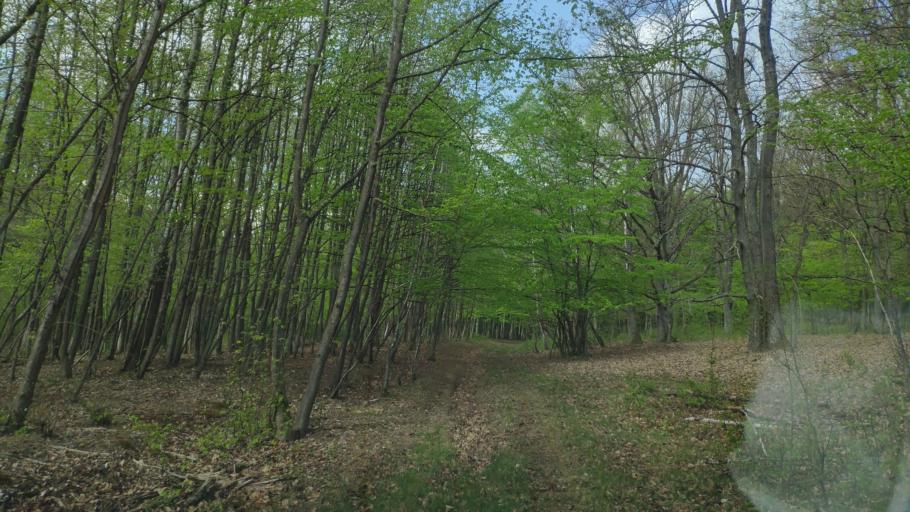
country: SK
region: Kosicky
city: Moldava nad Bodvou
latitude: 48.5380
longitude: 20.9421
